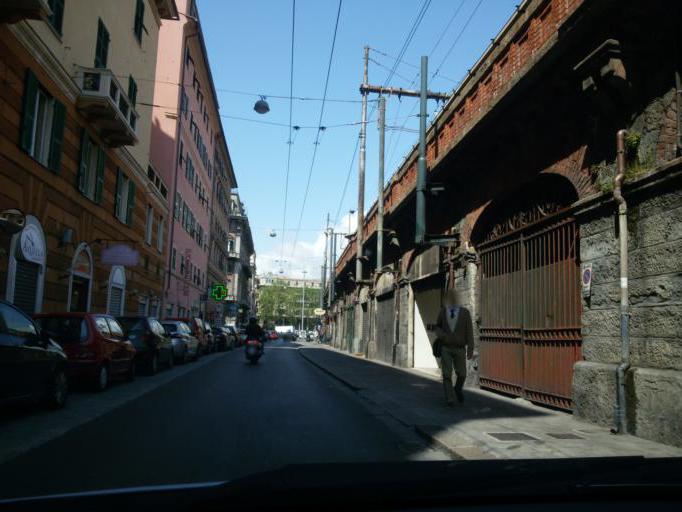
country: IT
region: Liguria
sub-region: Provincia di Genova
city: San Teodoro
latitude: 44.4109
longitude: 8.8910
